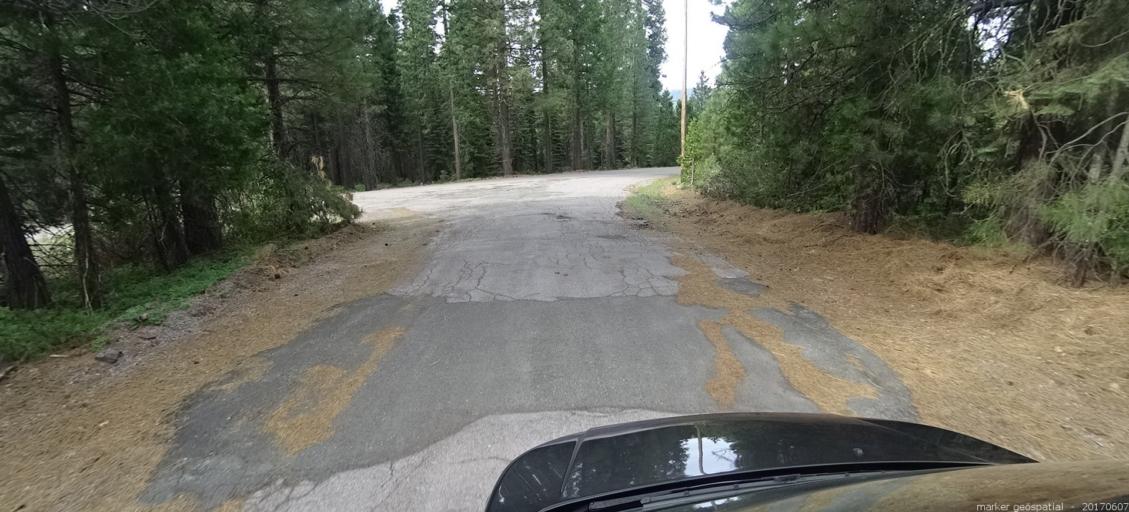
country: US
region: California
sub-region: Shasta County
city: Burney
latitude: 41.1976
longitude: -121.6869
